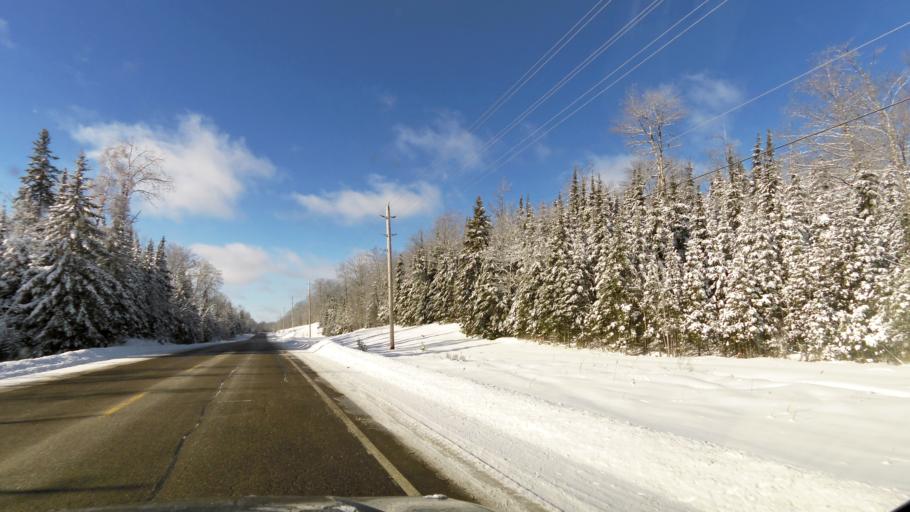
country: CA
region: Ontario
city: Bancroft
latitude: 45.0117
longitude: -78.3233
